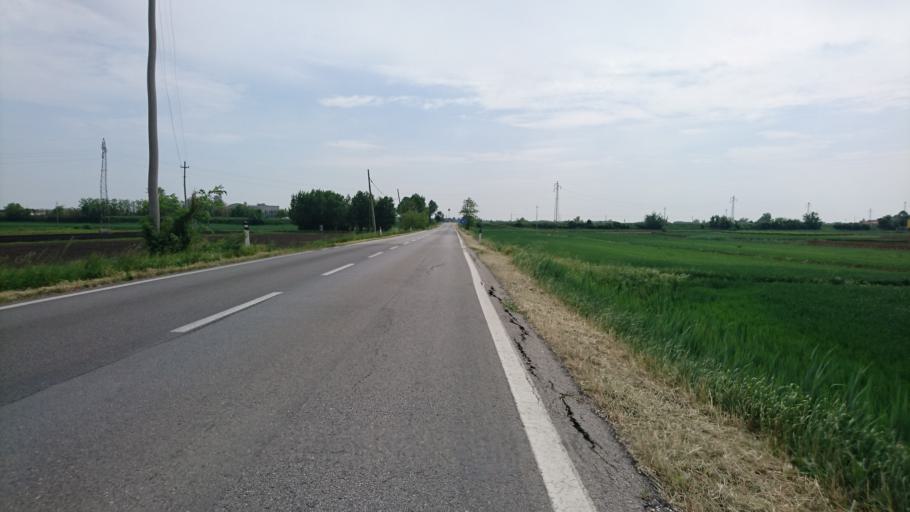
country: IT
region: Veneto
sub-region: Provincia di Padova
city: Arqua Petrarca
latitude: 45.2519
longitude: 11.7164
